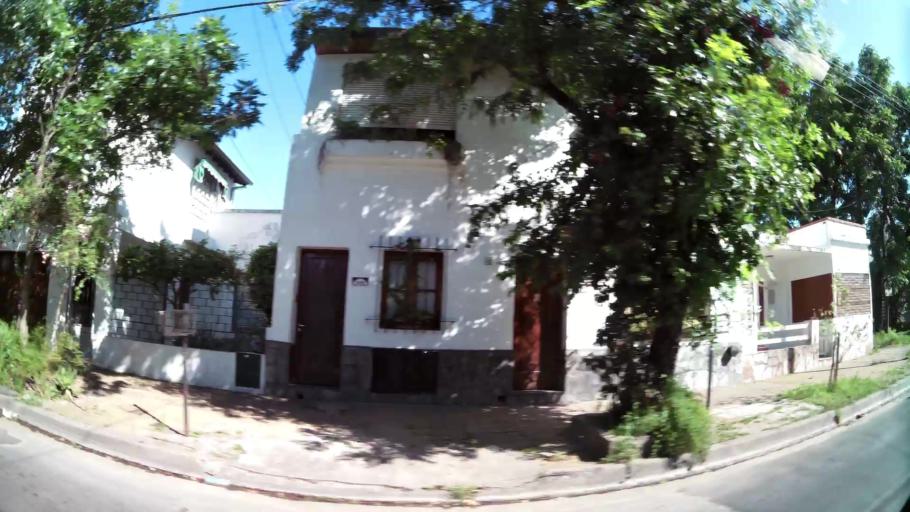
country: AR
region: Buenos Aires
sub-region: Partido de San Isidro
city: San Isidro
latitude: -34.4583
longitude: -58.5364
